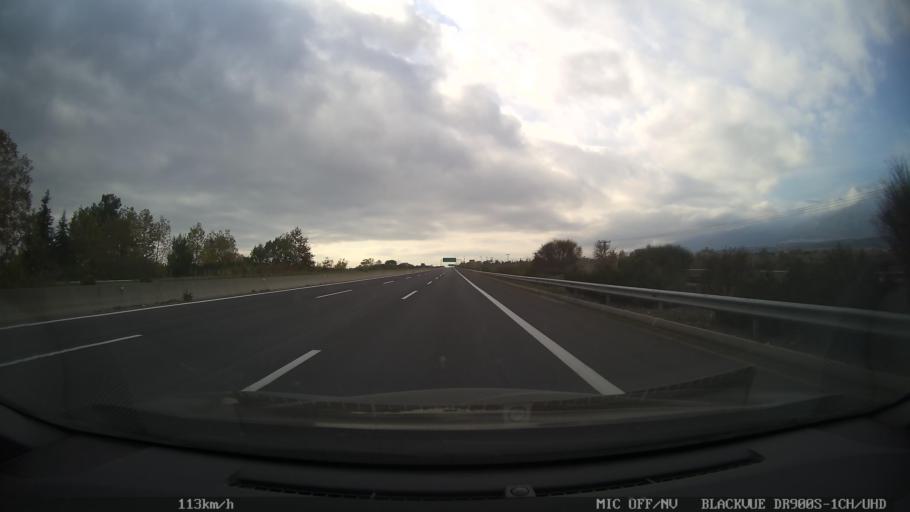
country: GR
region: Central Macedonia
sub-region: Nomos Pierias
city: Litochoro
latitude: 40.1453
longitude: 22.5416
